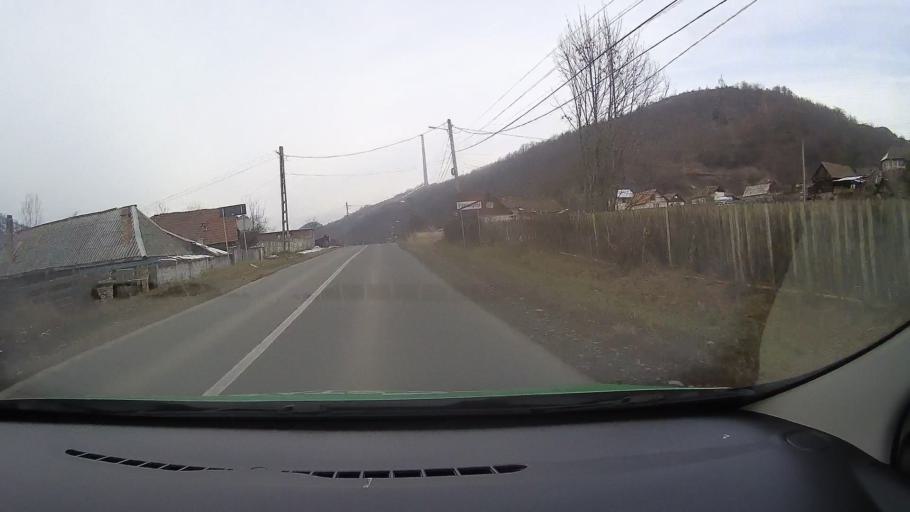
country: RO
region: Alba
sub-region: Oras Zlatna
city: Zlatna
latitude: 46.1014
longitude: 23.2489
